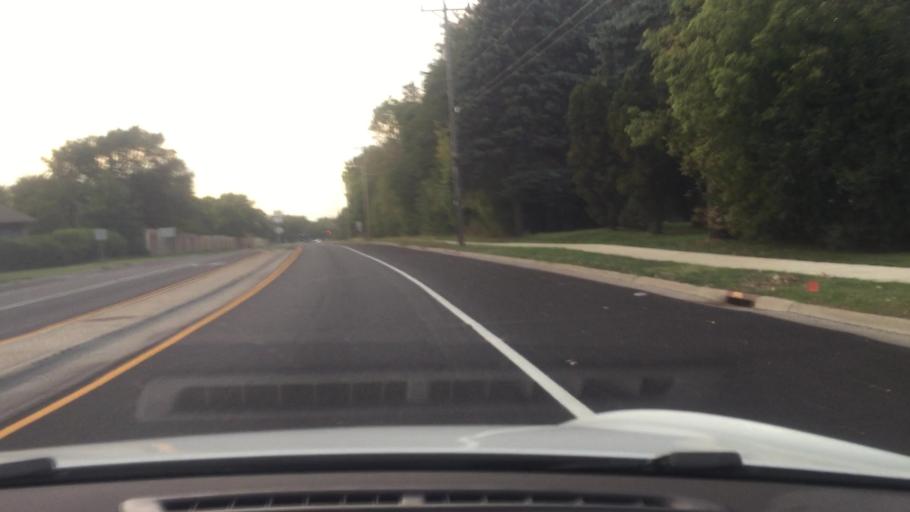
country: US
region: Minnesota
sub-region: Ramsey County
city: Shoreview
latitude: 45.0867
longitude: -93.1211
